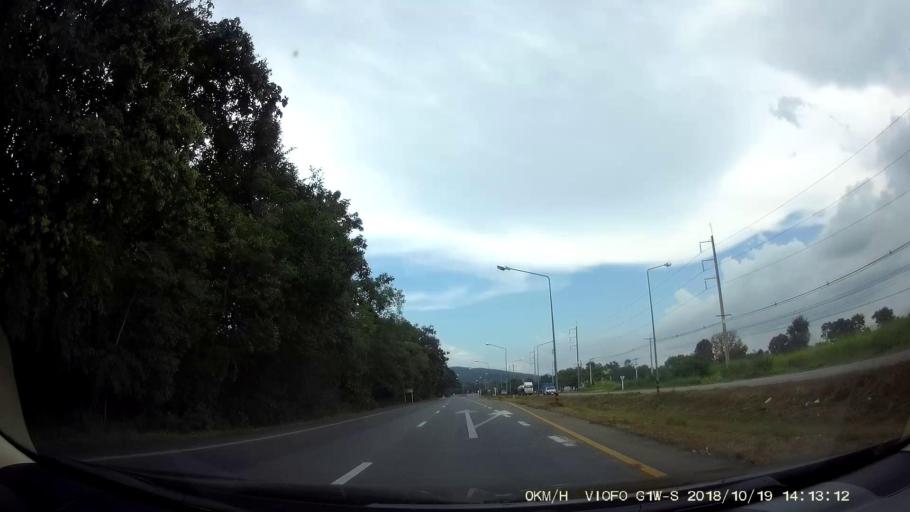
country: TH
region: Chaiyaphum
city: Khon Sawan
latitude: 15.9584
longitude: 102.1790
